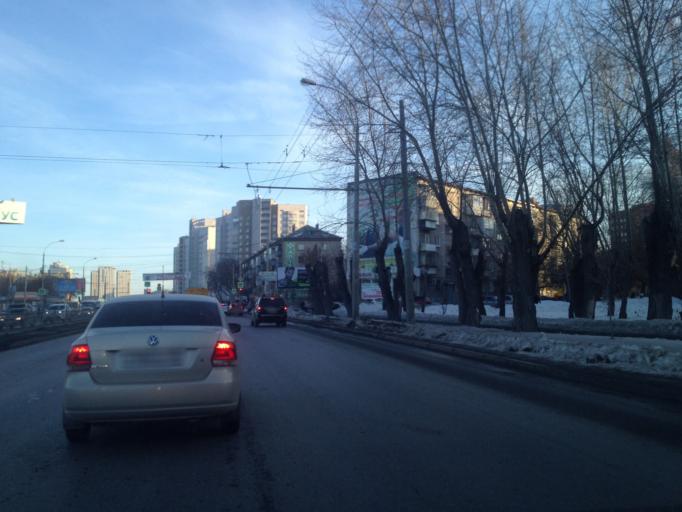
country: RU
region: Sverdlovsk
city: Yekaterinburg
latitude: 56.7881
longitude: 60.6470
